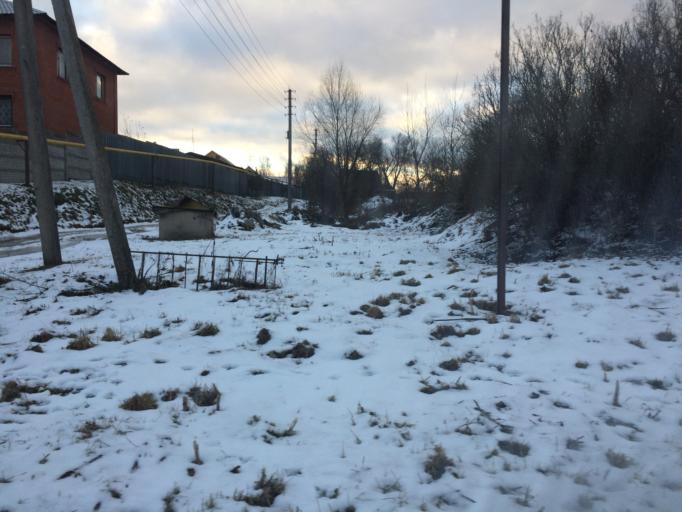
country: RU
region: Tula
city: Cherepet'
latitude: 54.1161
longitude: 36.3489
